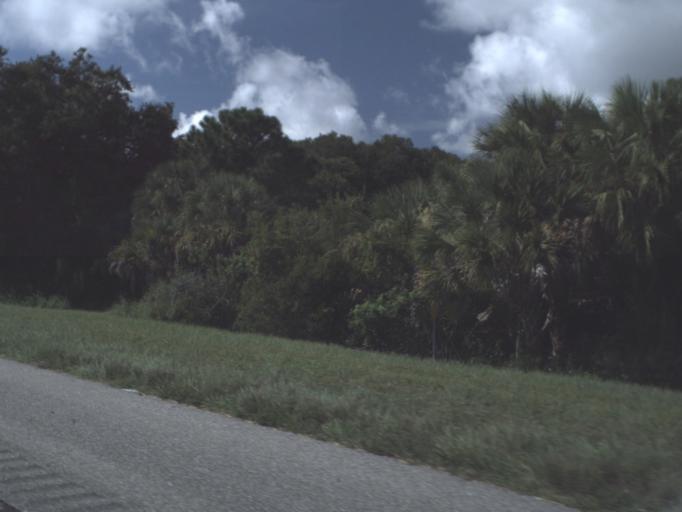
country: US
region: Florida
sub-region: Sarasota County
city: Vamo
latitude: 27.2258
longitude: -82.4516
